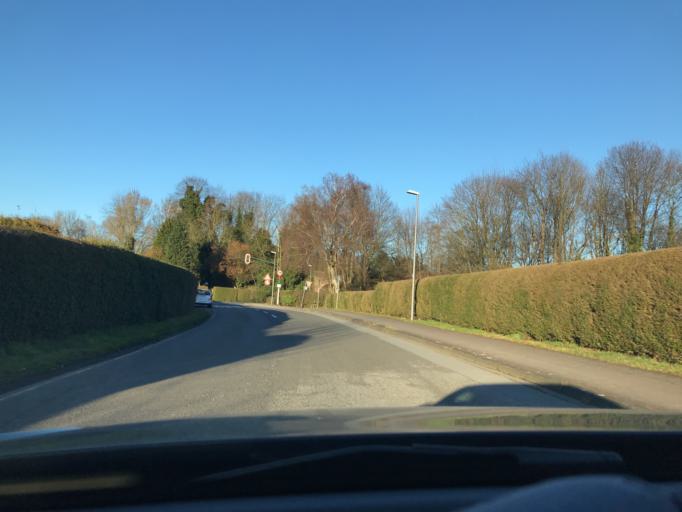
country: DE
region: North Rhine-Westphalia
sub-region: Regierungsbezirk Dusseldorf
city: Krefeld
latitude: 51.3158
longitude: 6.5440
